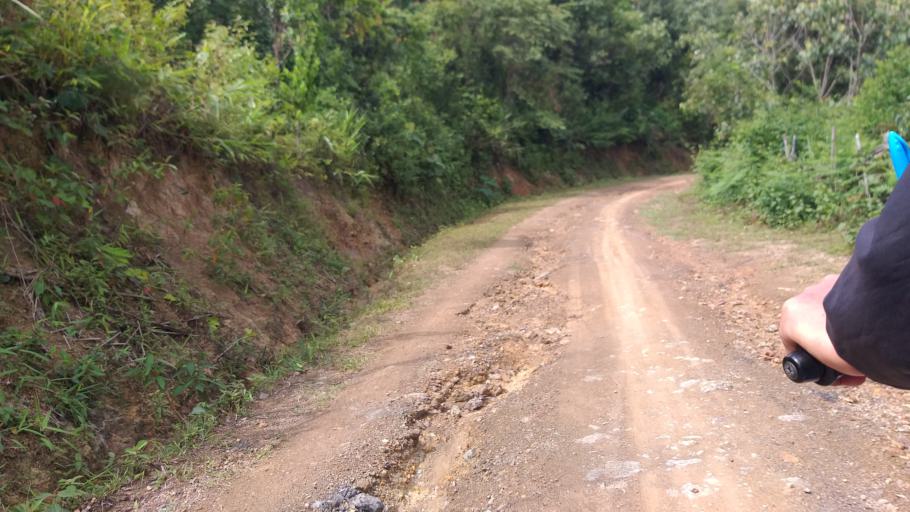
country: VN
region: Huyen Dien Bien
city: Dien Bien Phu
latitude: 21.4852
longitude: 102.6817
